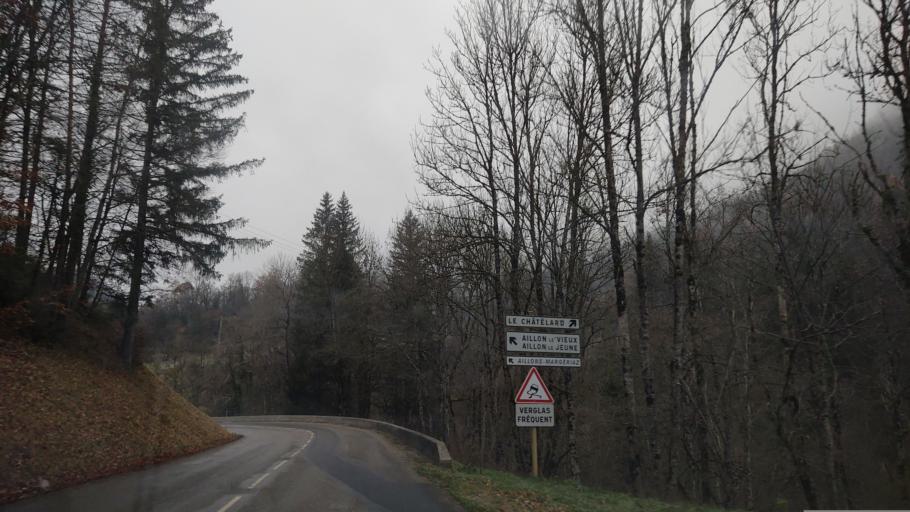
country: FR
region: Rhone-Alpes
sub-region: Departement de la Haute-Savoie
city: Doussard
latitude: 45.6731
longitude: 6.1446
